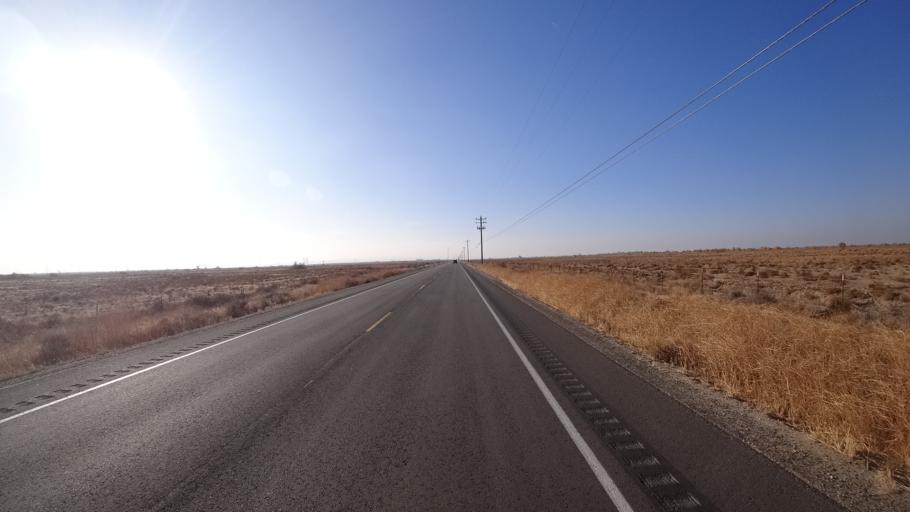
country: US
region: California
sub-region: Kern County
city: Rosedale
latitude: 35.2962
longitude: -119.2175
